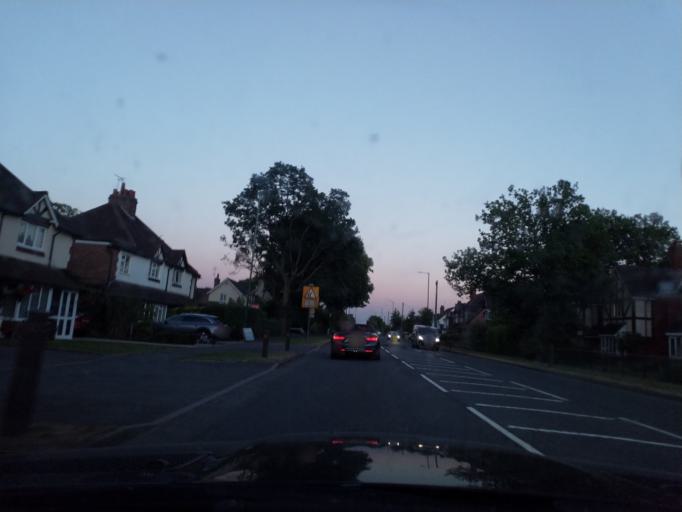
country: GB
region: England
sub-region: Solihull
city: Balsall Common
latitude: 52.3977
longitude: -1.6543
